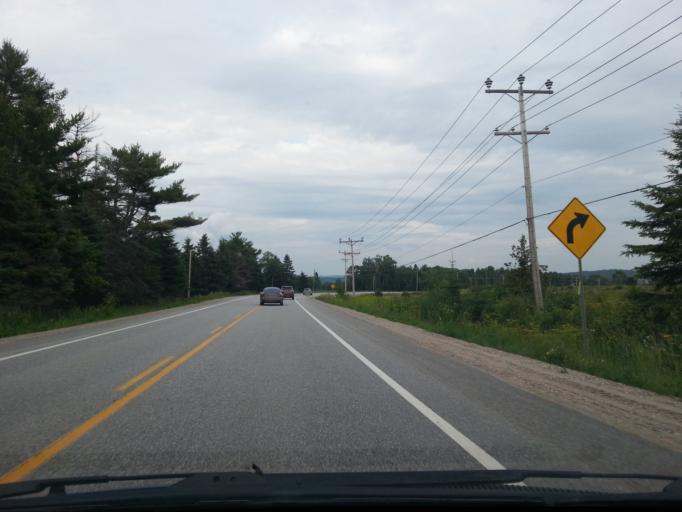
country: CA
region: Quebec
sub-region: Outaouais
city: Maniwaki
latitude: 46.0422
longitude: -76.0553
